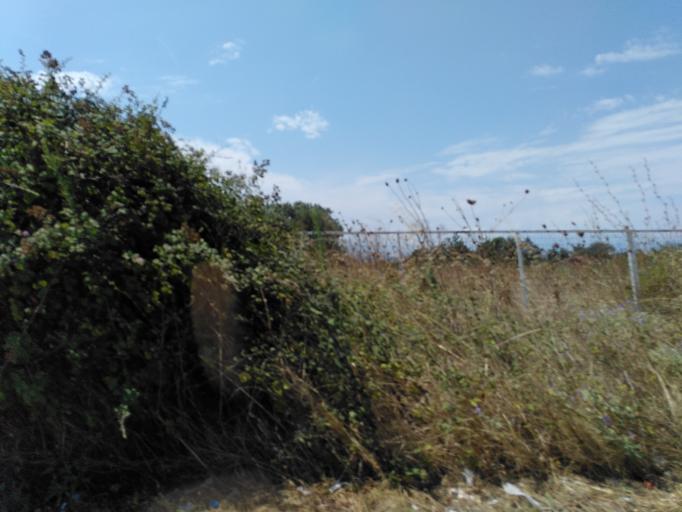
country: GR
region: Central Macedonia
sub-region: Nomos Thessalonikis
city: Nea Michaniona
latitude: 40.4808
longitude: 22.8689
